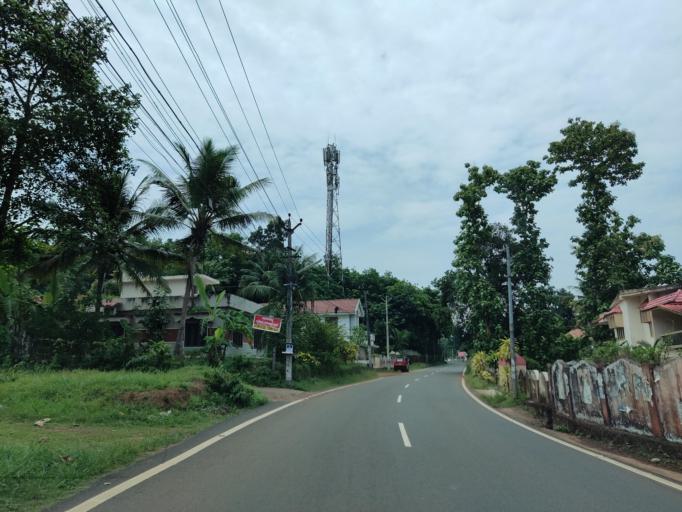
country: IN
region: Kerala
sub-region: Alappuzha
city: Chengannur
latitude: 9.2922
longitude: 76.6192
